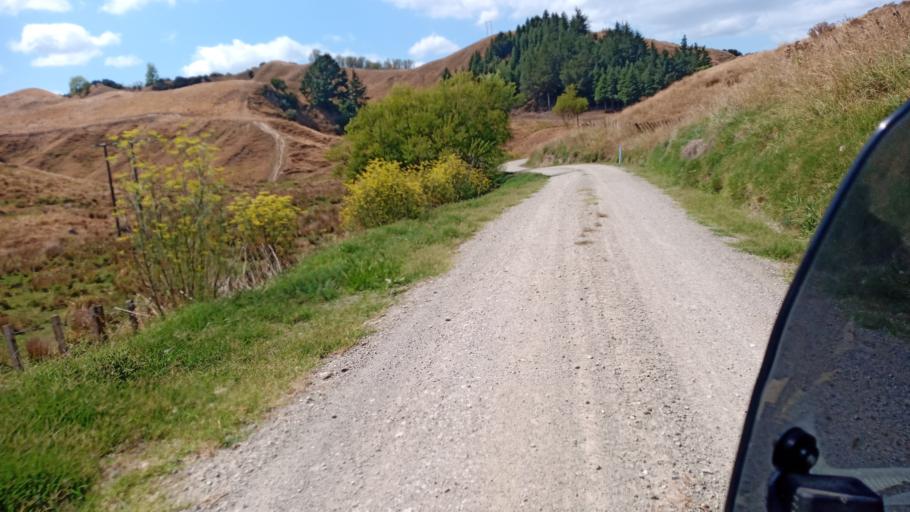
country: NZ
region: Gisborne
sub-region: Gisborne District
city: Gisborne
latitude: -38.4902
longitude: 177.8482
